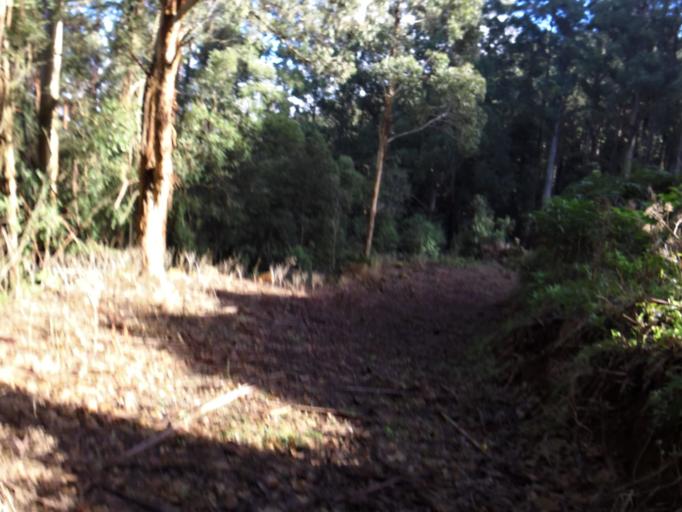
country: AU
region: Victoria
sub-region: Yarra Ranges
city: Mount Dandenong
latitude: -37.8399
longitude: 145.3510
